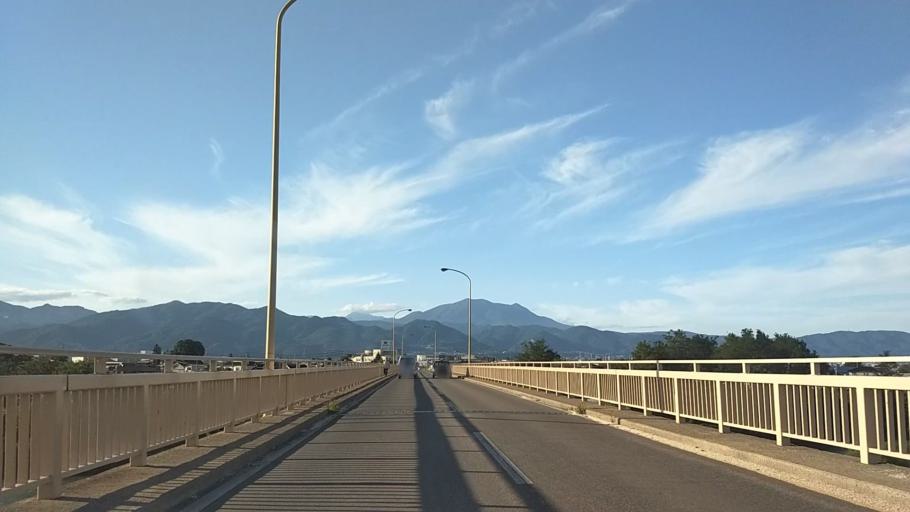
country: JP
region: Nagano
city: Nagano-shi
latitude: 36.5953
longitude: 138.1965
